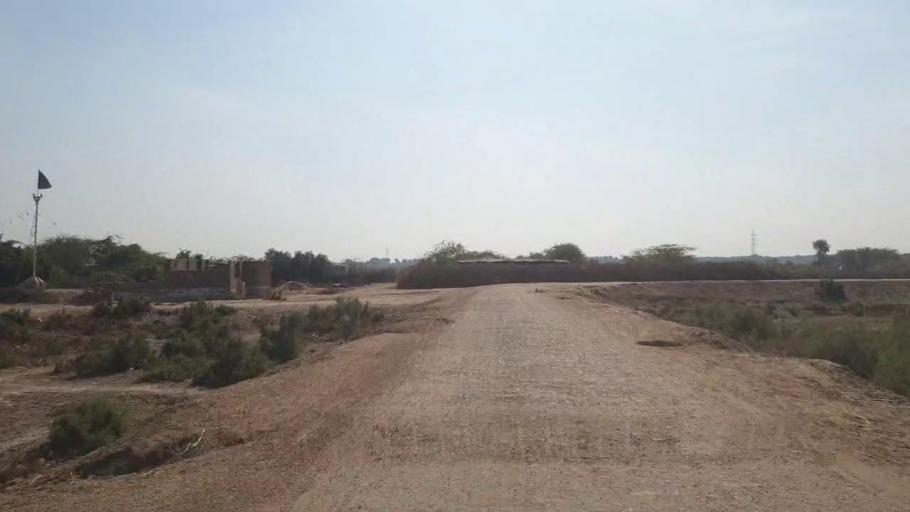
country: PK
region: Sindh
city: Chambar
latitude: 25.3326
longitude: 68.8047
